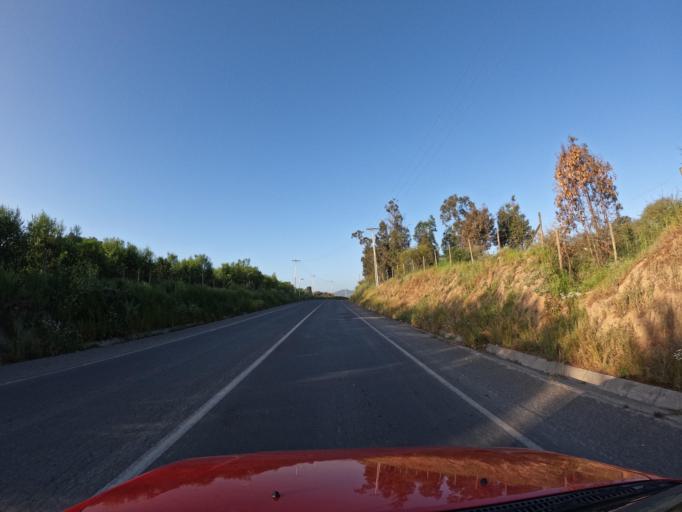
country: CL
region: O'Higgins
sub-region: Provincia de Colchagua
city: Santa Cruz
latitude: -34.3202
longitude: -71.3891
